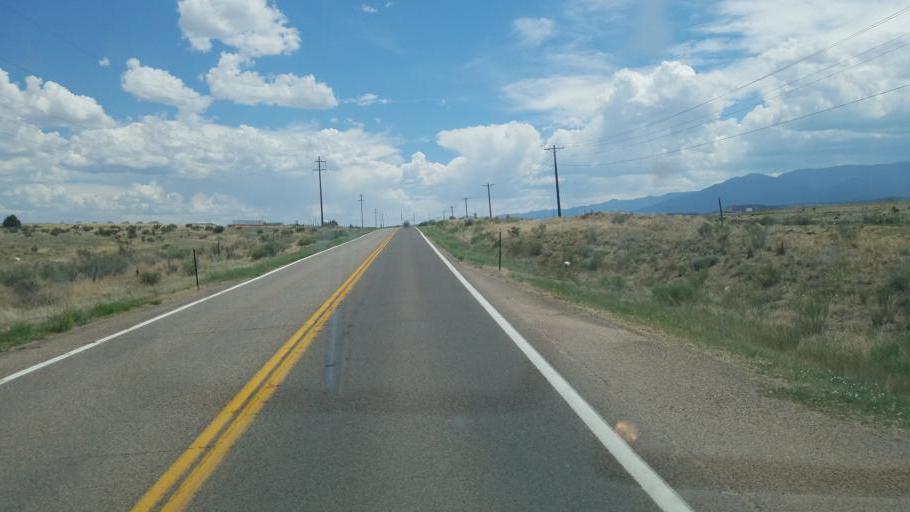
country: US
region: Colorado
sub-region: Fremont County
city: Florence
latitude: 38.3732
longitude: -105.1093
